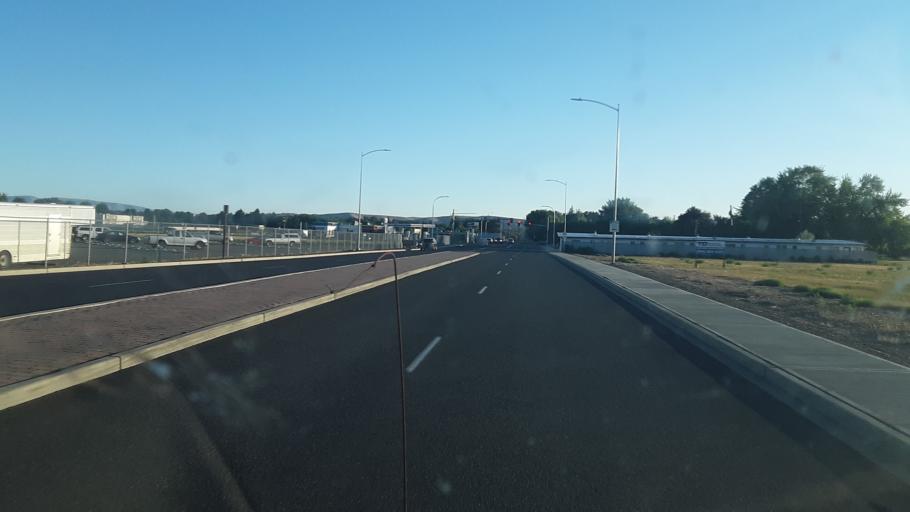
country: US
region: Washington
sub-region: Yakima County
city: Yakima
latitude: 46.5690
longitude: -120.5301
